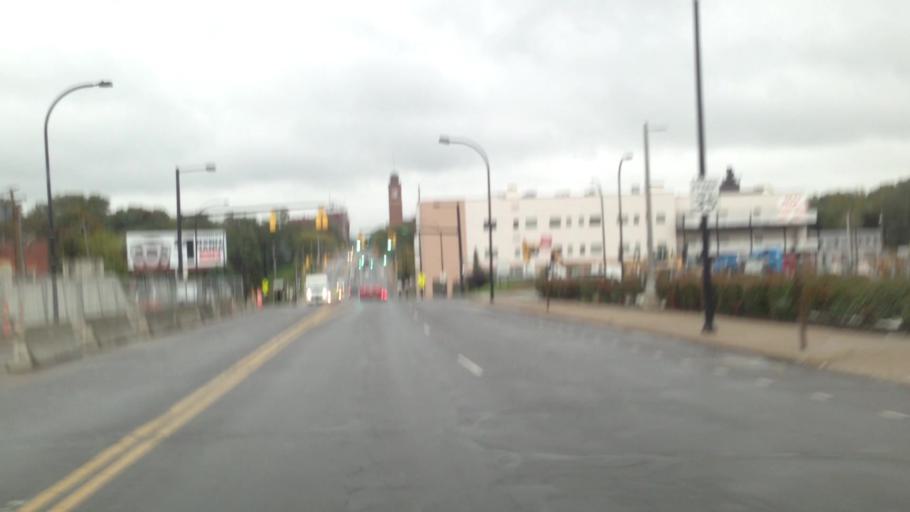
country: US
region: Ohio
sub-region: Summit County
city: Akron
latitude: 41.0718
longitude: -81.4899
